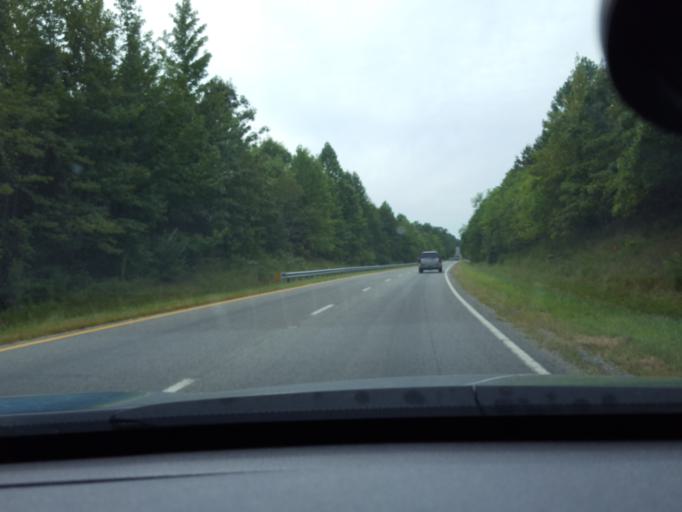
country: US
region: Virginia
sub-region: Caroline County
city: Bowling Green
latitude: 38.1003
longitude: -77.2739
